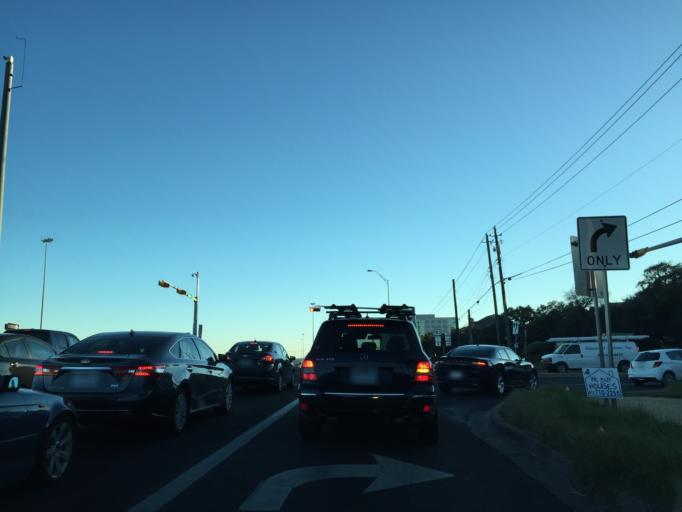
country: US
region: Texas
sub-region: Williamson County
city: Jollyville
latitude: 30.3904
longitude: -97.7349
